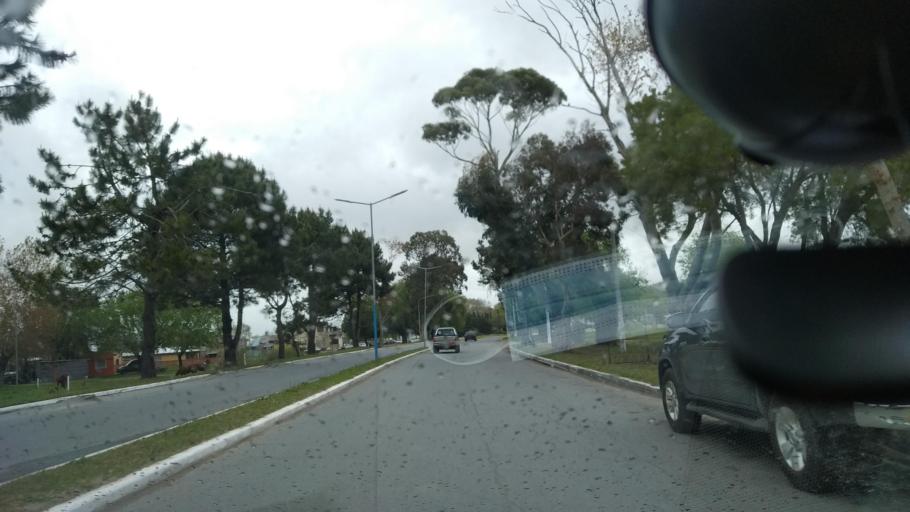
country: AR
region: Buenos Aires
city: San Clemente del Tuyu
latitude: -36.3846
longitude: -56.7254
